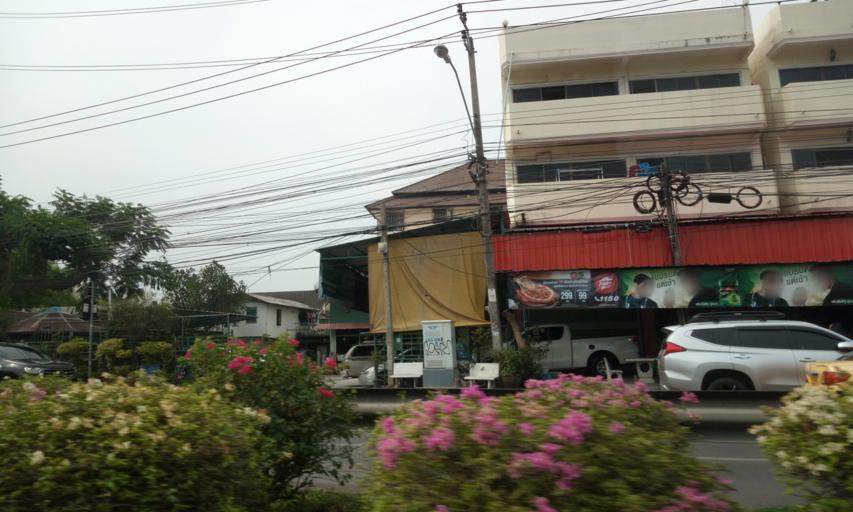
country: TH
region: Bangkok
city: Lat Krabang
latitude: 13.7223
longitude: 100.7527
